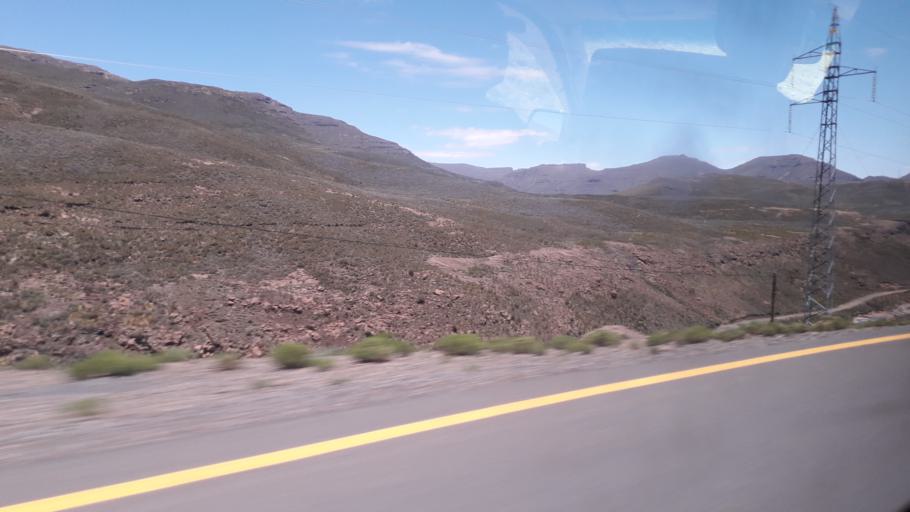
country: ZA
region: Orange Free State
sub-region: Thabo Mofutsanyana District Municipality
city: Phuthaditjhaba
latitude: -28.7662
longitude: 28.6590
